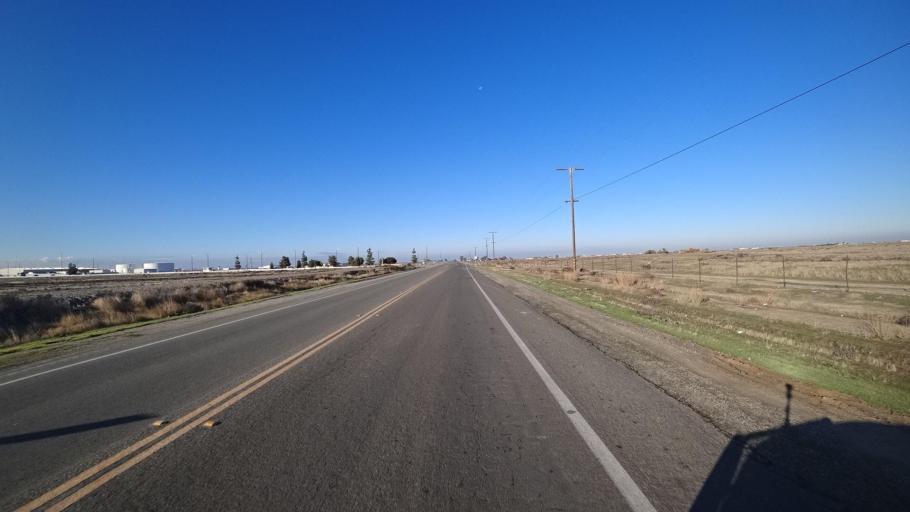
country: US
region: California
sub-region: Kern County
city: Delano
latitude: 35.7758
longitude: -119.3191
